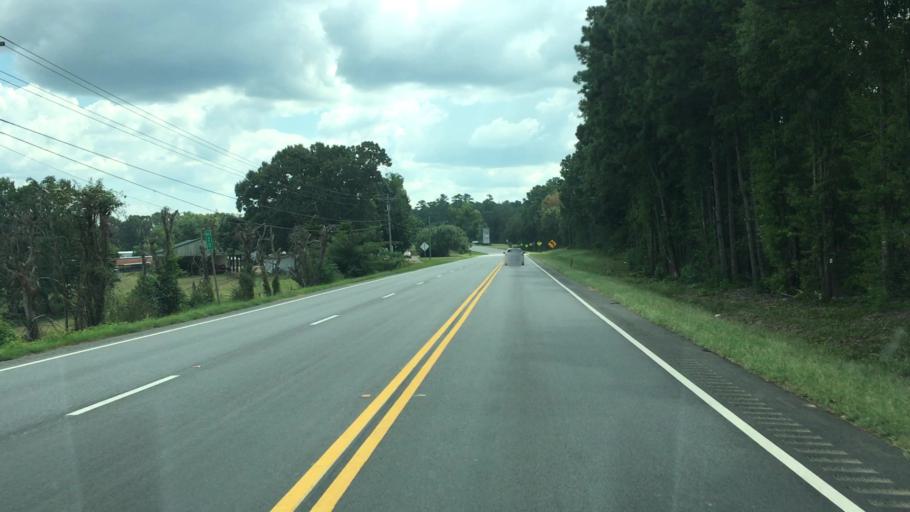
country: US
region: Georgia
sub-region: Putnam County
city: Jefferson
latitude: 33.4219
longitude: -83.3709
